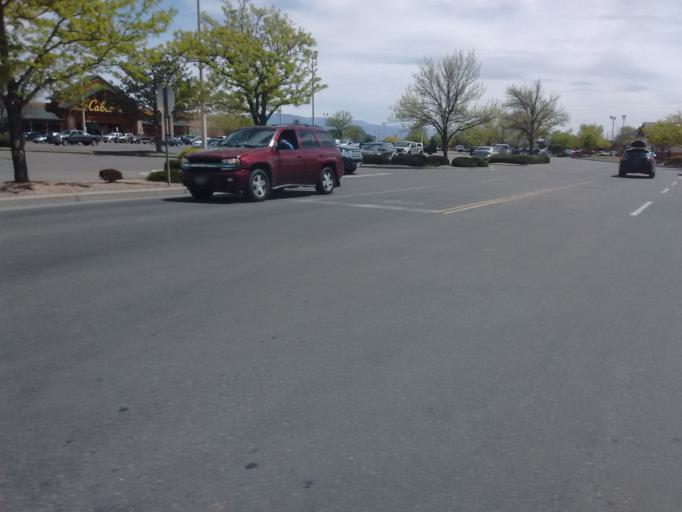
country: US
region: Colorado
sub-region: Mesa County
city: Redlands
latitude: 39.0905
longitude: -108.6043
